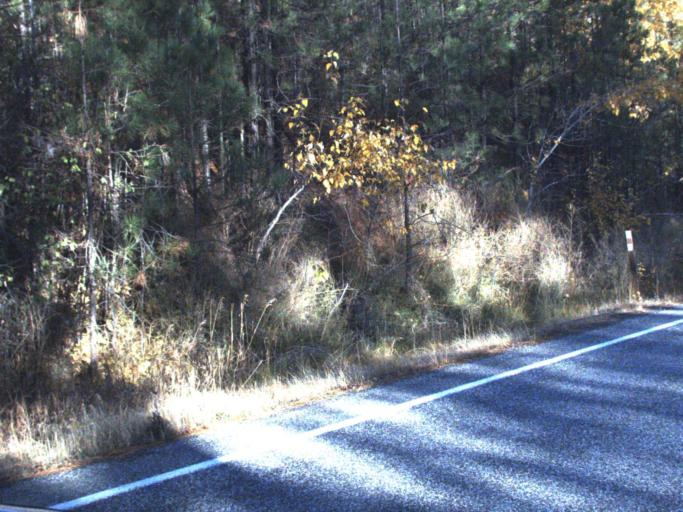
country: US
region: Washington
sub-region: Okanogan County
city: Coulee Dam
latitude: 48.0352
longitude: -118.6738
